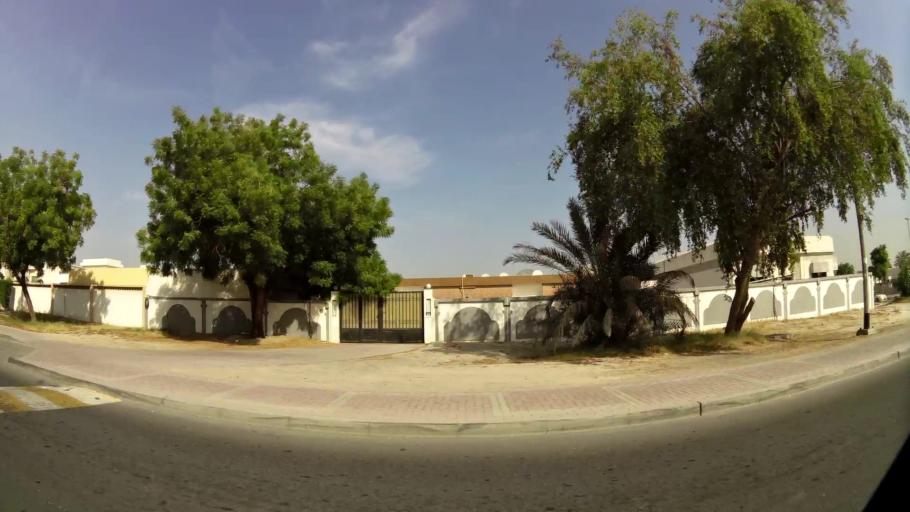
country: AE
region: Ash Shariqah
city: Sharjah
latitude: 25.2244
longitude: 55.3895
